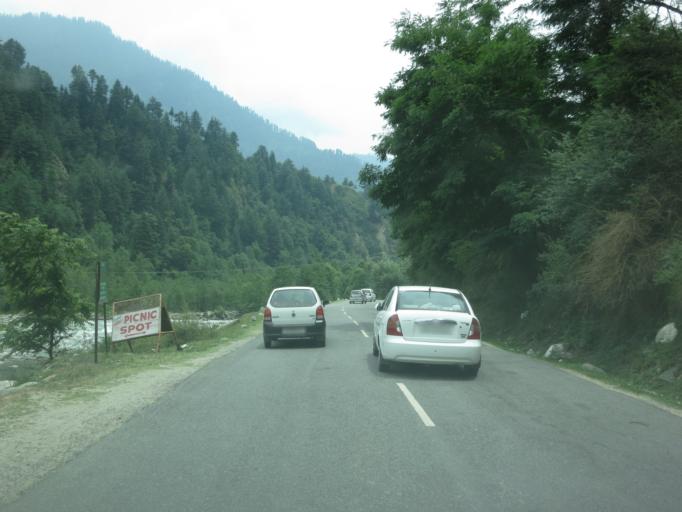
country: IN
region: Himachal Pradesh
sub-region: Kulu
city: Nagar
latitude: 32.1752
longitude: 77.1798
